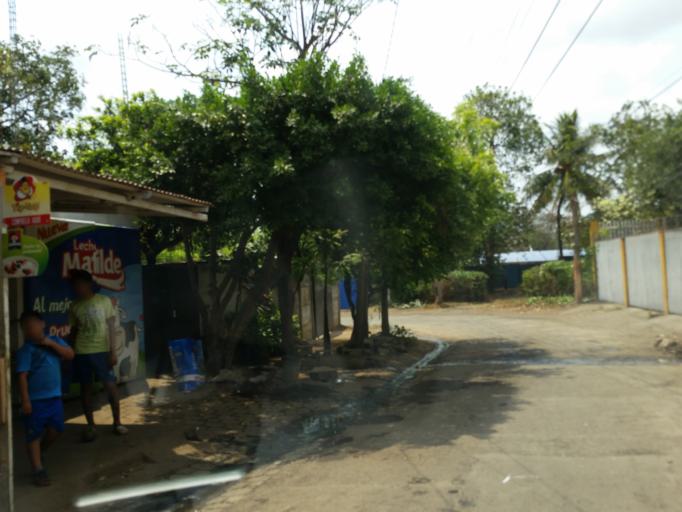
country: NI
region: Managua
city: Managua
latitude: 12.0812
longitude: -86.2309
